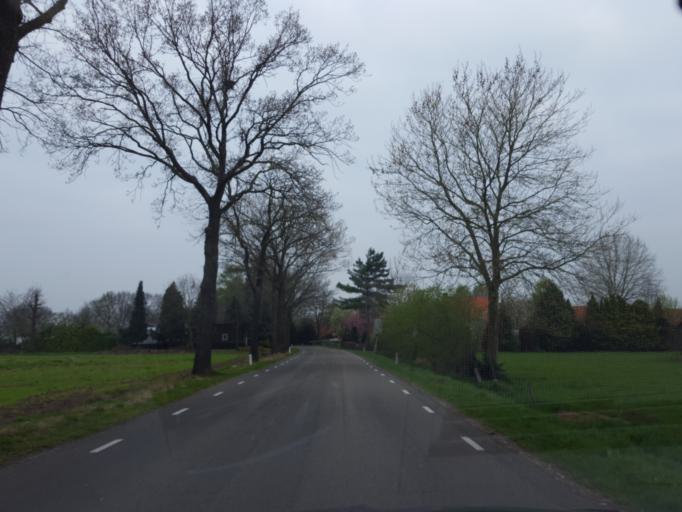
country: NL
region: Limburg
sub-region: Gemeente Nederweert
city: Nederweert
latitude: 51.3182
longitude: 5.7013
